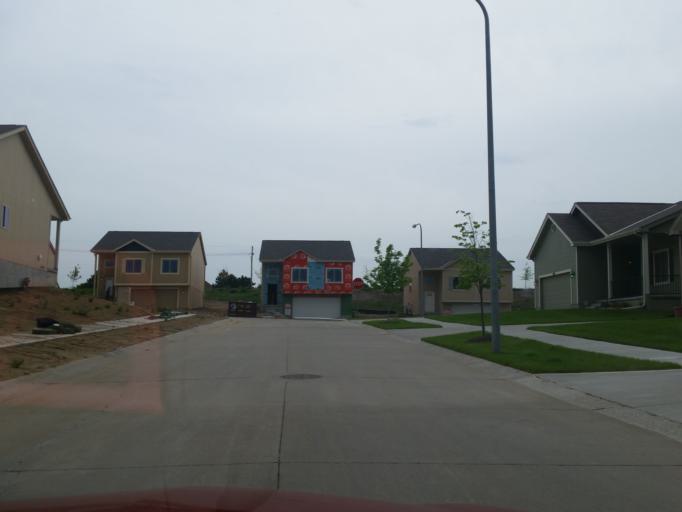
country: US
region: Nebraska
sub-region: Douglas County
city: Bennington
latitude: 41.3223
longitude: -96.1306
